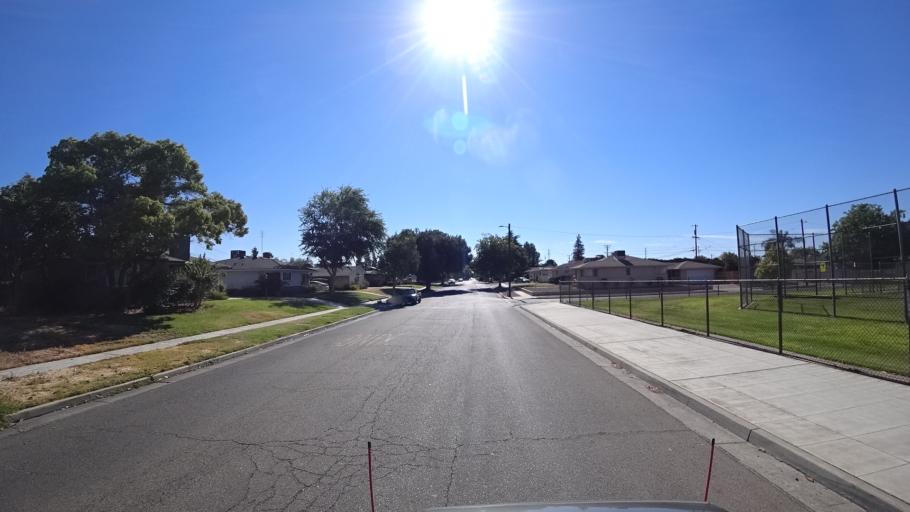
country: US
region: California
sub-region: Fresno County
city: Fresno
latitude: 36.7756
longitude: -119.8294
